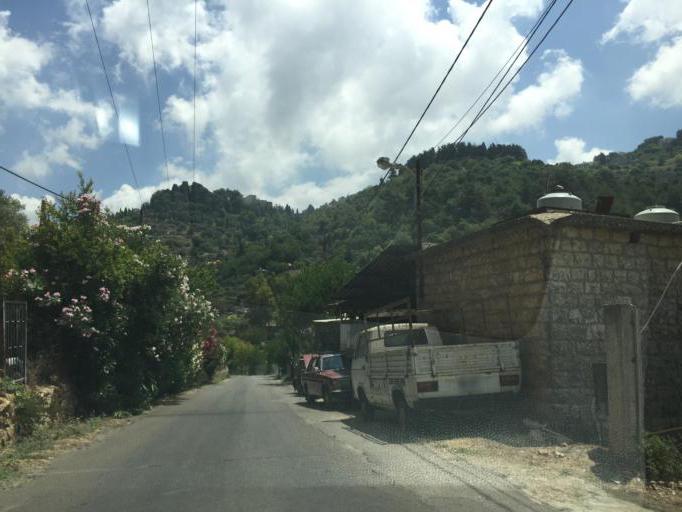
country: LB
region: Mont-Liban
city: Beit ed Dine
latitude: 33.6951
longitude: 35.5722
